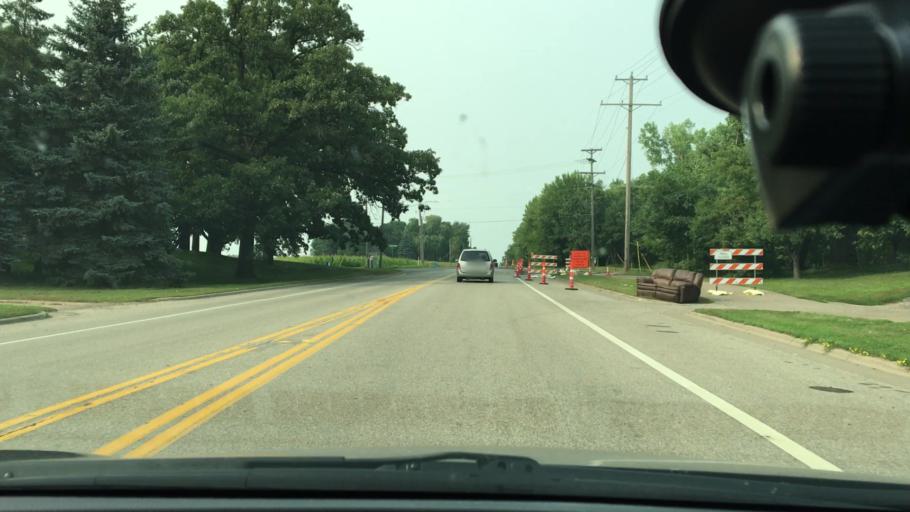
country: US
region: Minnesota
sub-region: Hennepin County
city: Osseo
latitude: 45.1421
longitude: -93.4621
